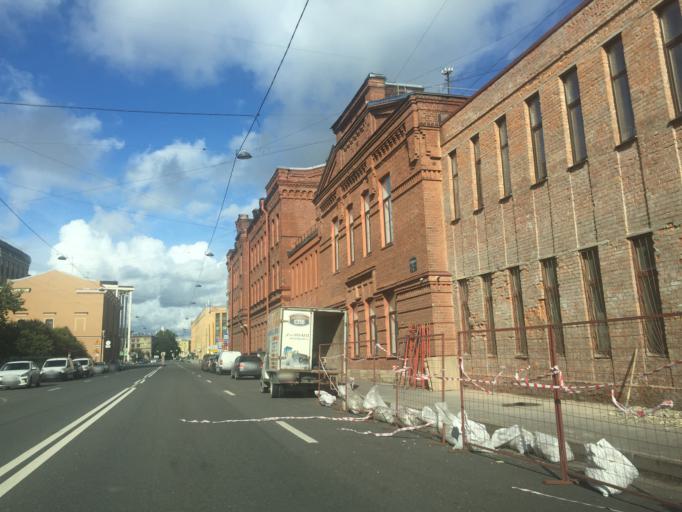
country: RU
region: St.-Petersburg
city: Centralniy
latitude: 59.9359
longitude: 30.3858
